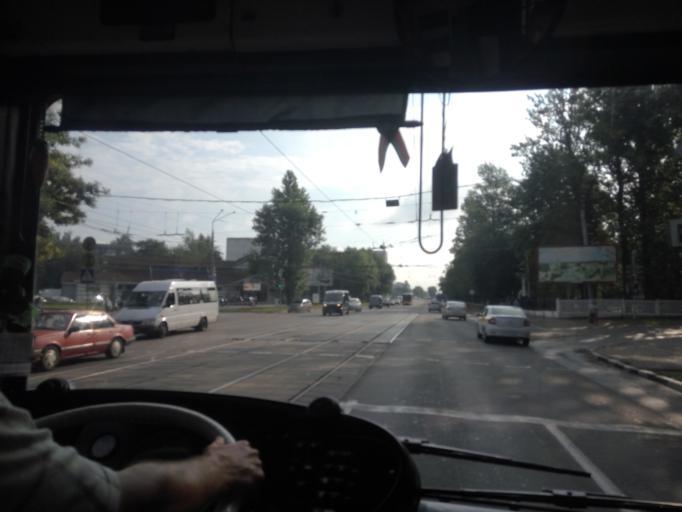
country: BY
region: Vitebsk
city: Vitebsk
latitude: 55.1951
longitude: 30.2427
